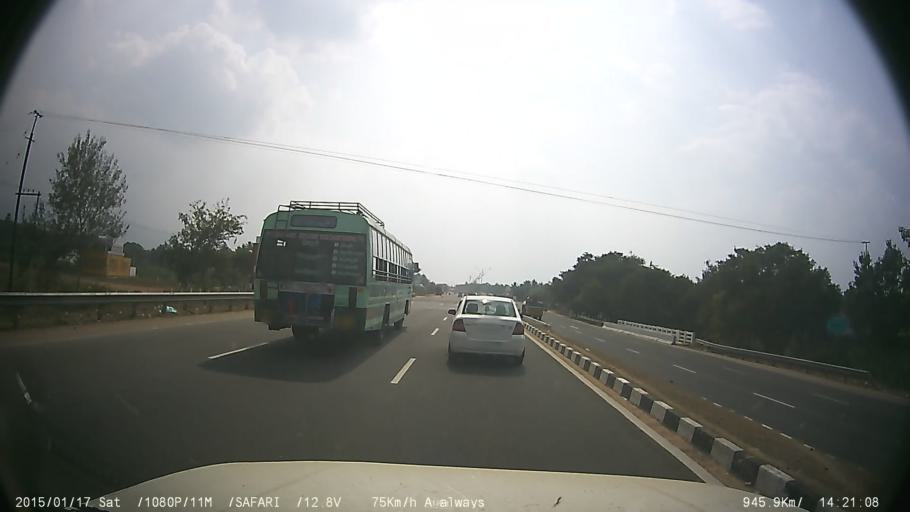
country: IN
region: Tamil Nadu
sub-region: Vellore
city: Vaniyambadi
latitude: 12.7012
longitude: 78.6441
